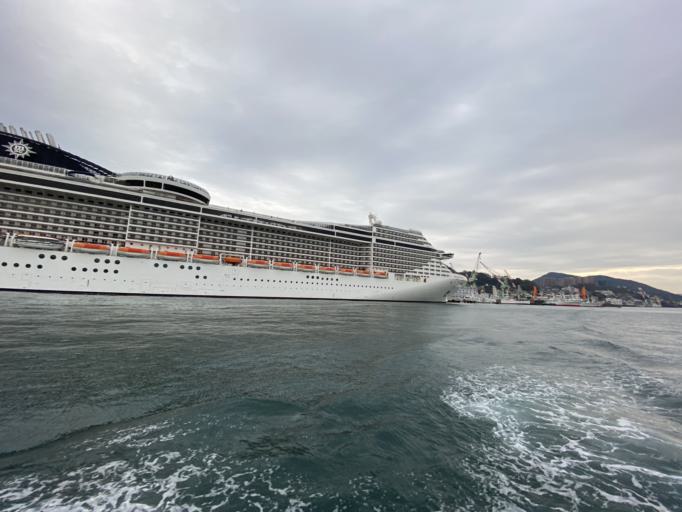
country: JP
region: Nagasaki
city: Nagasaki-shi
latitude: 32.7376
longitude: 129.8662
